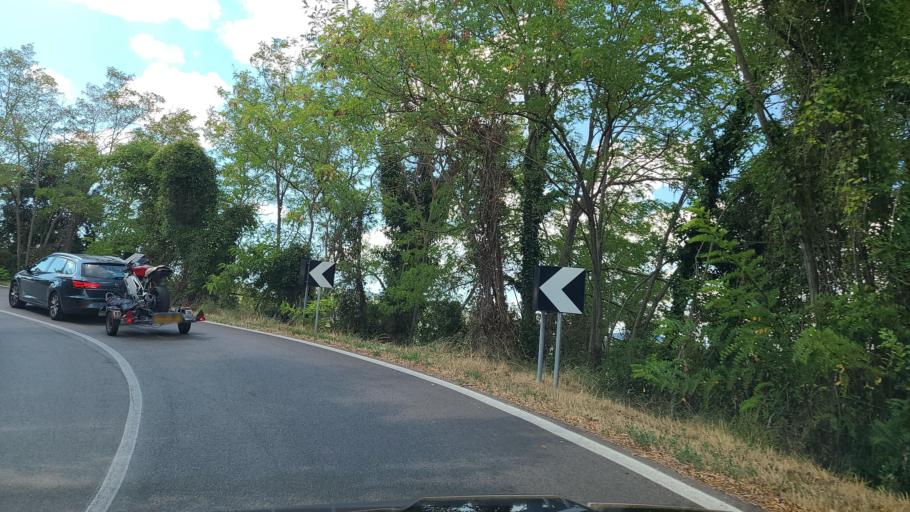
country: IT
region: Tuscany
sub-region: Provincia di Siena
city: San Gimignano
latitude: 43.4047
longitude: 11.0133
